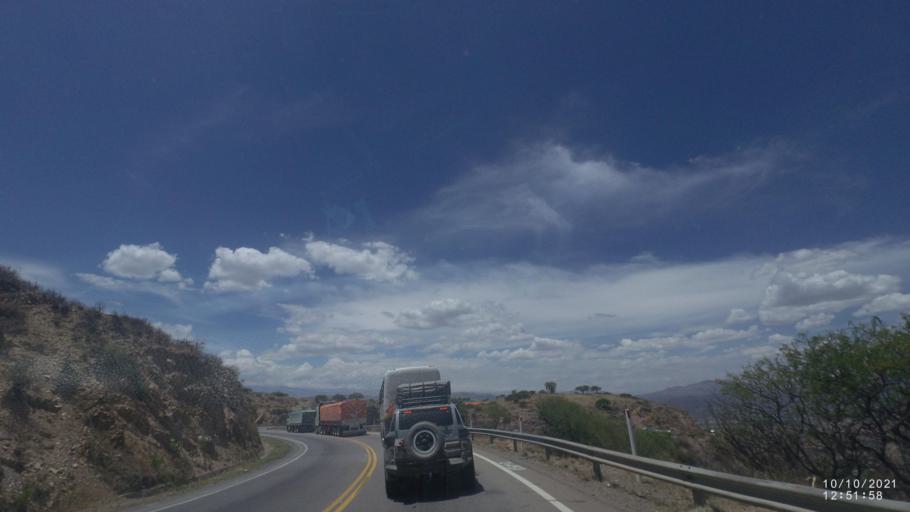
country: BO
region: Cochabamba
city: Irpa Irpa
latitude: -17.6158
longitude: -66.3606
